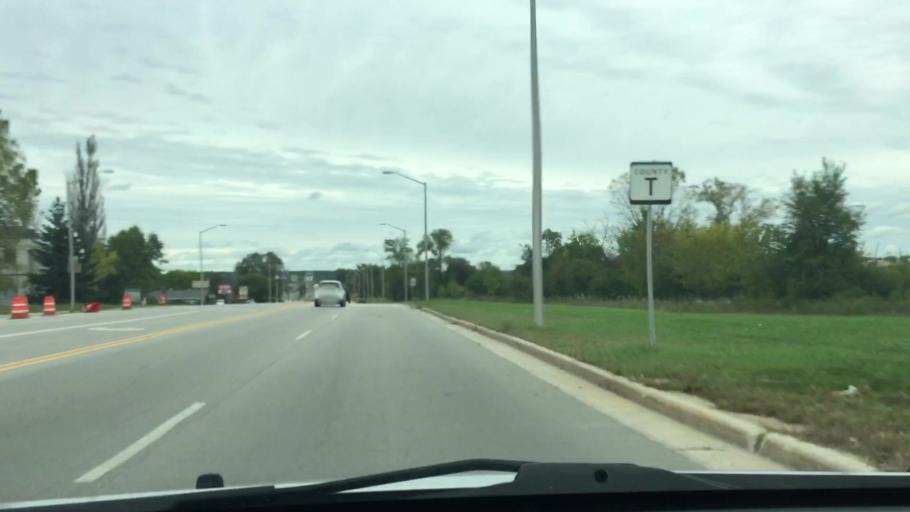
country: US
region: Wisconsin
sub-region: Waukesha County
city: Waukesha
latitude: 43.0325
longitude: -88.2559
